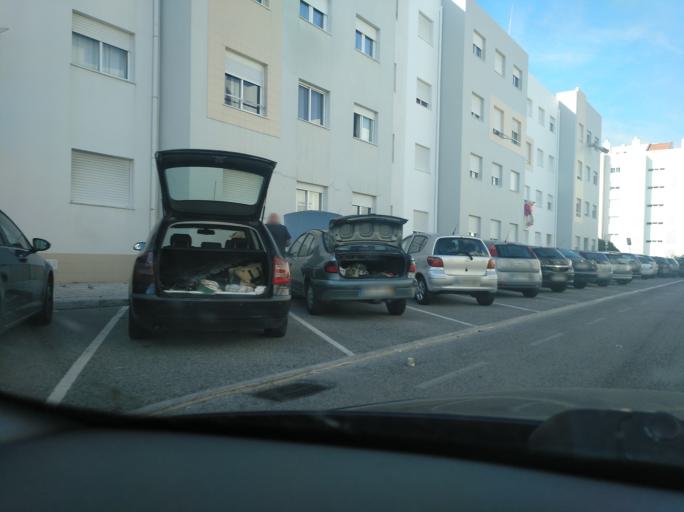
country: PT
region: Lisbon
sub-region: Oeiras
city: Linda-a-Velha
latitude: 38.7181
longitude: -9.2303
